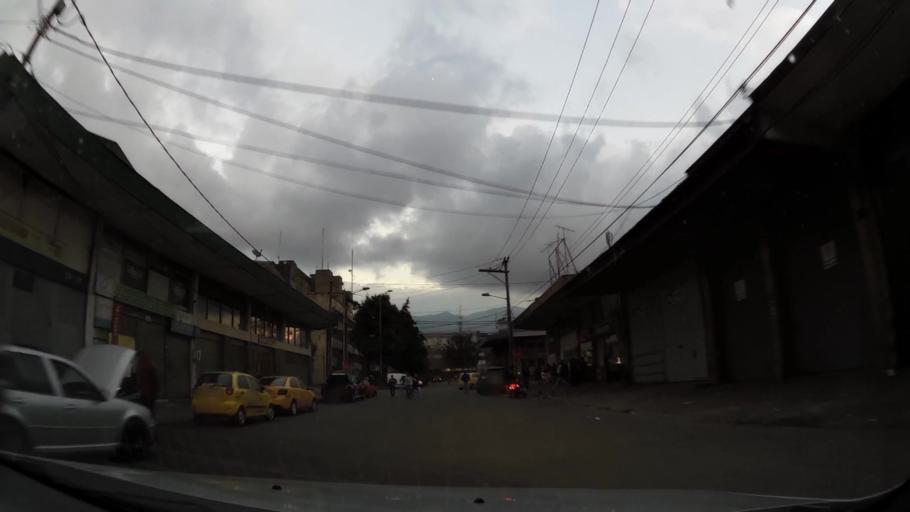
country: CO
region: Bogota D.C.
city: Bogota
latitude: 4.6160
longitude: -74.0887
